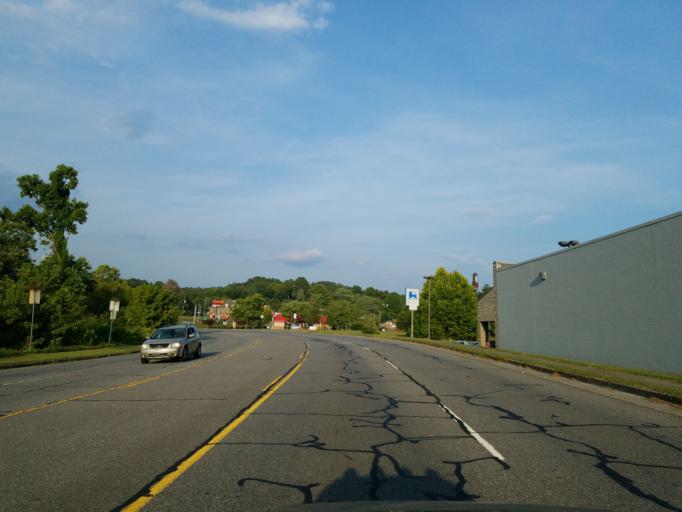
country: US
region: Georgia
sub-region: Gilmer County
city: Ellijay
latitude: 34.6849
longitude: -84.4766
